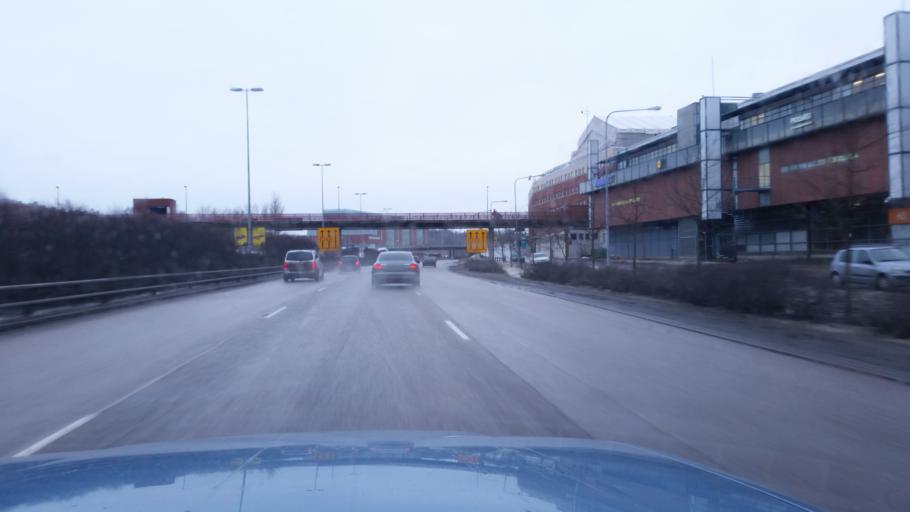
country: FI
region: Uusimaa
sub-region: Helsinki
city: Vantaa
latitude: 60.2100
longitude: 25.0810
